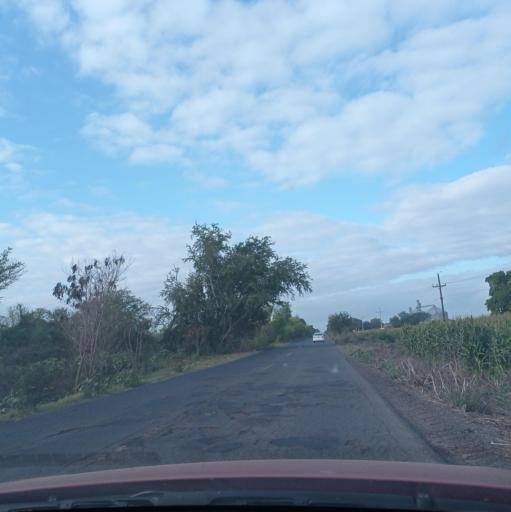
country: MX
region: Sinaloa
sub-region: Guasave
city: Las Quemazones
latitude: 25.6554
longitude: -108.5251
